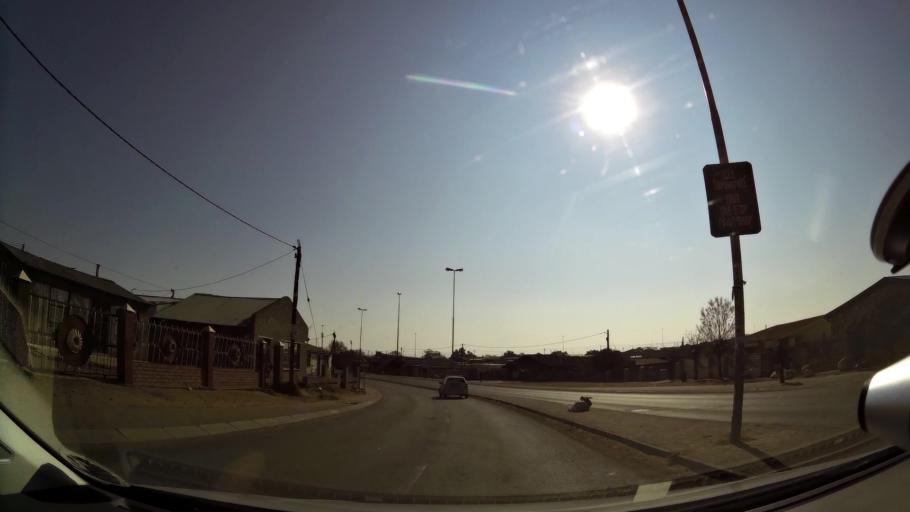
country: ZA
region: Orange Free State
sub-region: Mangaung Metropolitan Municipality
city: Bloemfontein
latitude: -29.1810
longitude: 26.2348
